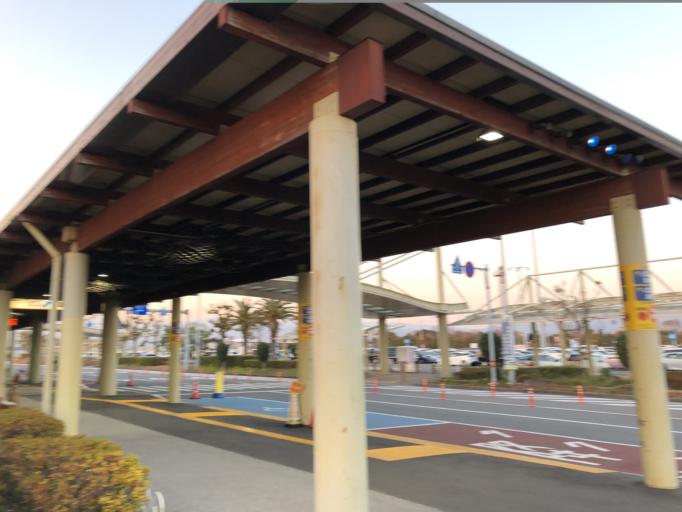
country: JP
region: Kochi
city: Kochi-shi
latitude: 33.5473
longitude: 133.6749
